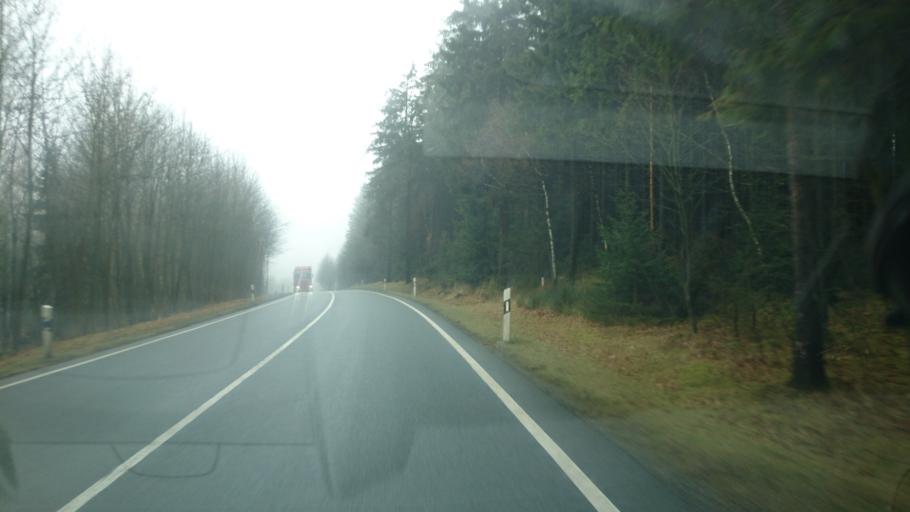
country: DE
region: Thuringia
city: Tanna
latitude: 50.4812
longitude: 11.8378
